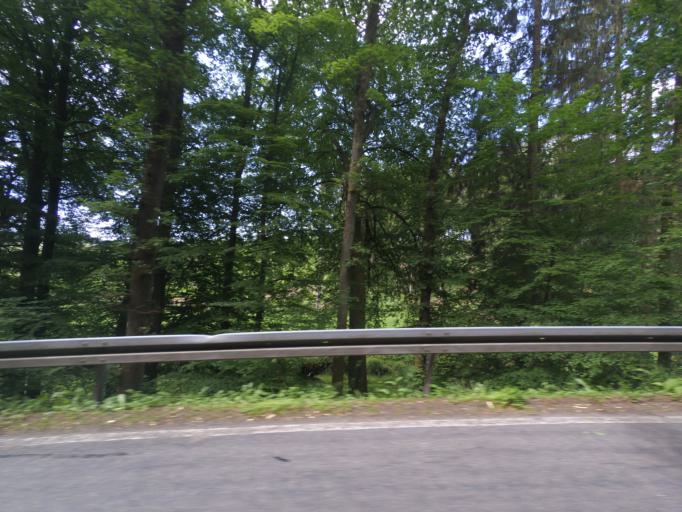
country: DE
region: Hesse
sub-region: Regierungsbezirk Darmstadt
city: Wald-Michelbach
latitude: 49.6199
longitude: 8.8419
